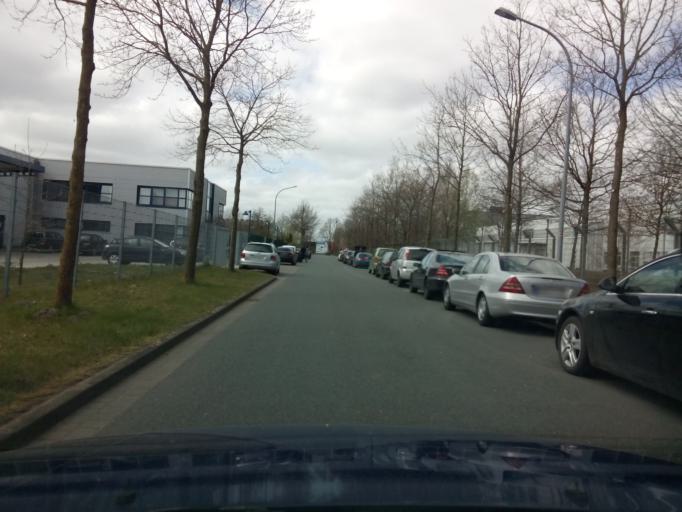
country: DE
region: Lower Saxony
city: Ritterhude
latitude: 53.2292
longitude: 8.7014
